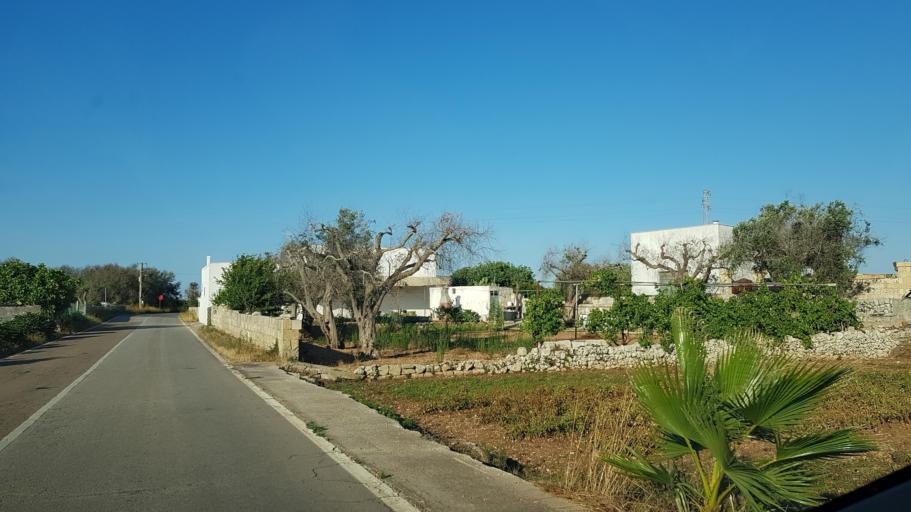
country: IT
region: Apulia
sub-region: Provincia di Lecce
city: Marittima
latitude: 40.0009
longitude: 18.4081
